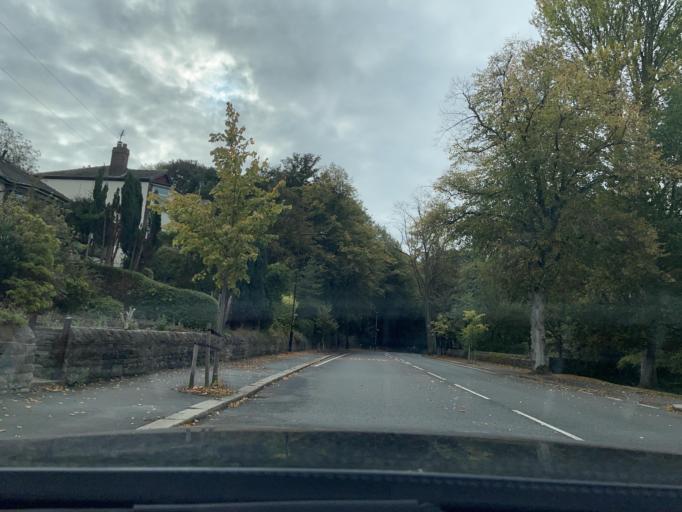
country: GB
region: England
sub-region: Sheffield
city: Oughtibridge
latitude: 53.3979
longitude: -1.5116
